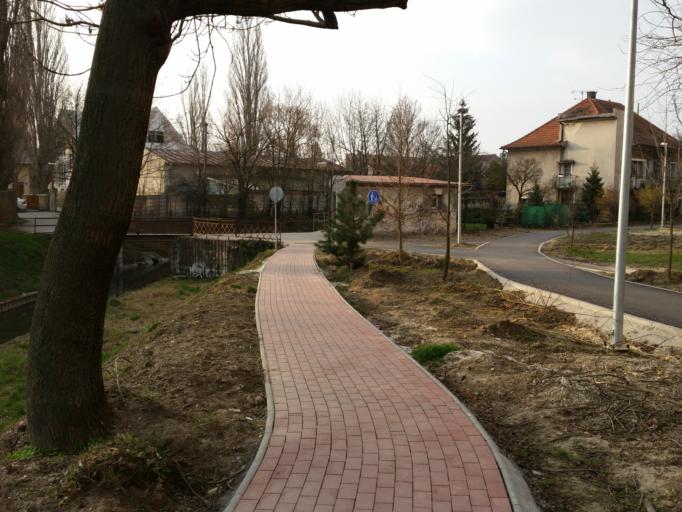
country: SK
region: Trnavsky
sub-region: Okres Trnava
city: Piestany
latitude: 48.5936
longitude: 17.8266
